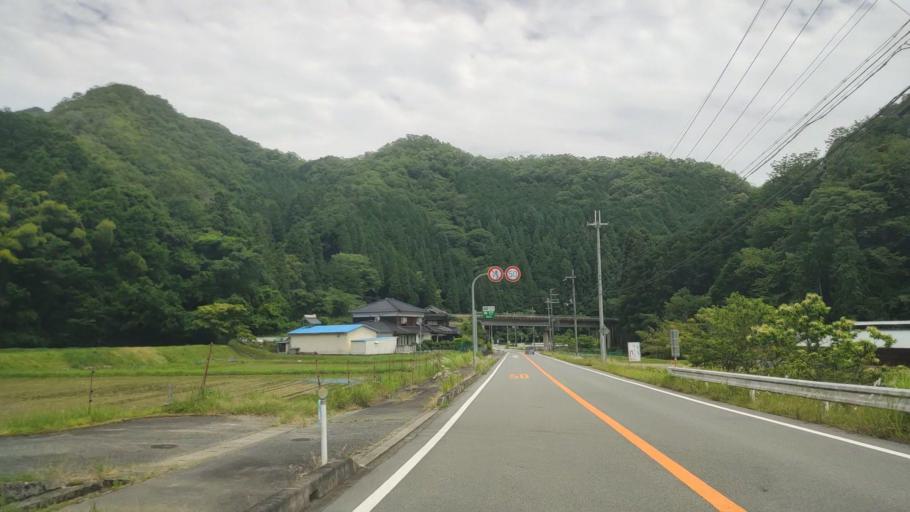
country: JP
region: Hyogo
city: Yamazakicho-nakabirose
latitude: 35.0721
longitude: 134.3578
